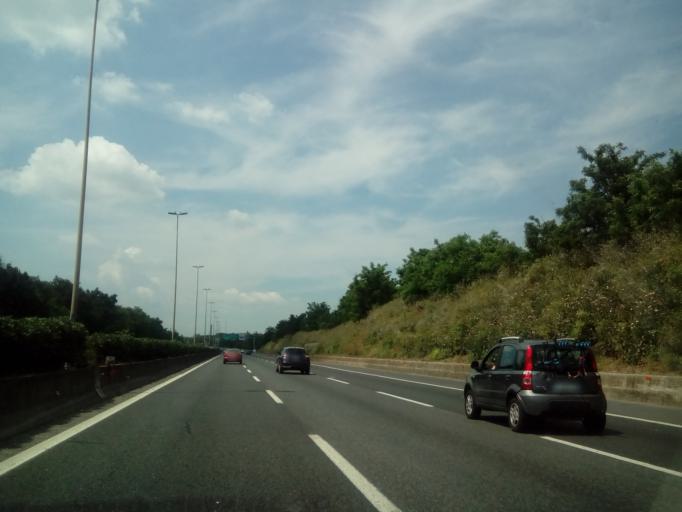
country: IT
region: Latium
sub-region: Citta metropolitana di Roma Capitale
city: Colle Verde
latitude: 41.9516
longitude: 12.5869
